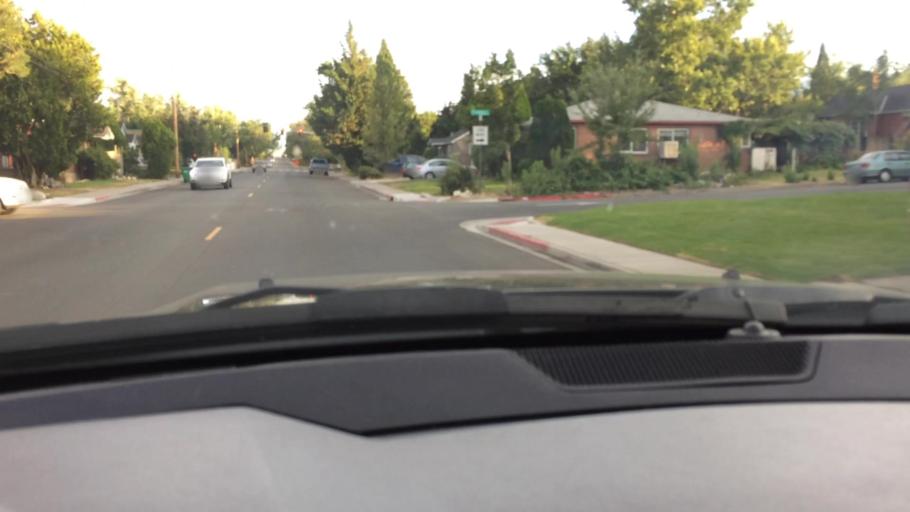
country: US
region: Nevada
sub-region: Washoe County
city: Reno
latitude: 39.5108
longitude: -119.8127
